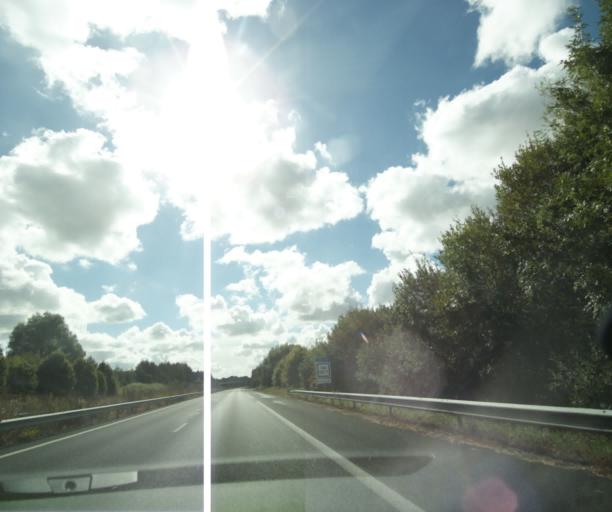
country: FR
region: Poitou-Charentes
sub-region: Departement de la Charente-Maritime
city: Cabariot
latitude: 45.9399
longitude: -0.8453
